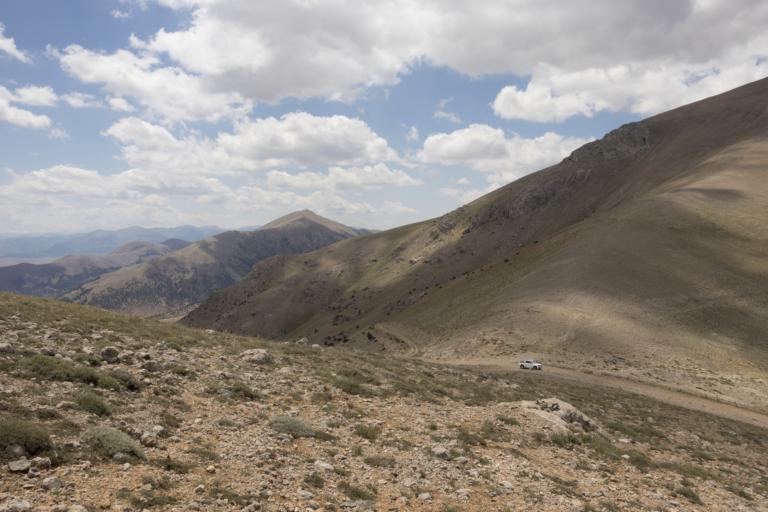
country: TR
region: Adana
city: Tufanbeyli
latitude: 38.3139
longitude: 36.0976
